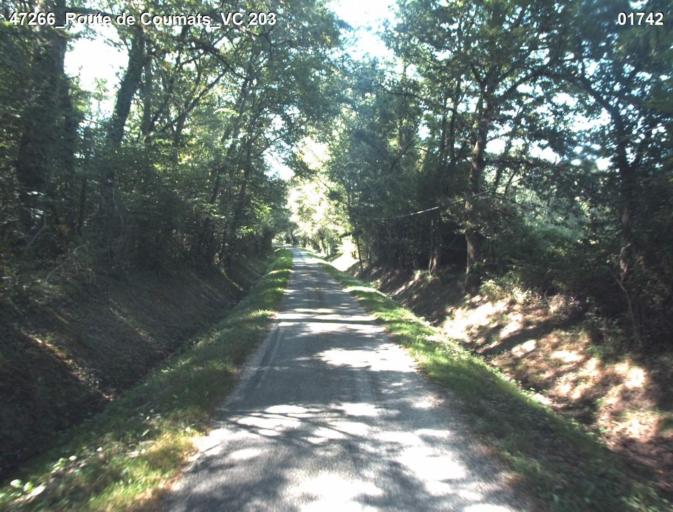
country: FR
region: Aquitaine
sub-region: Departement des Landes
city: Gabarret
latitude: 44.0043
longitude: 0.0969
